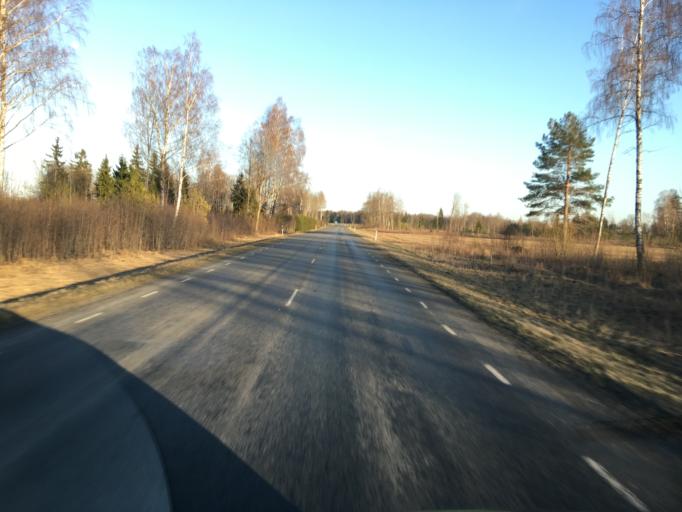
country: EE
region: Raplamaa
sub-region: Kehtna vald
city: Kehtna
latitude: 59.0612
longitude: 24.9363
